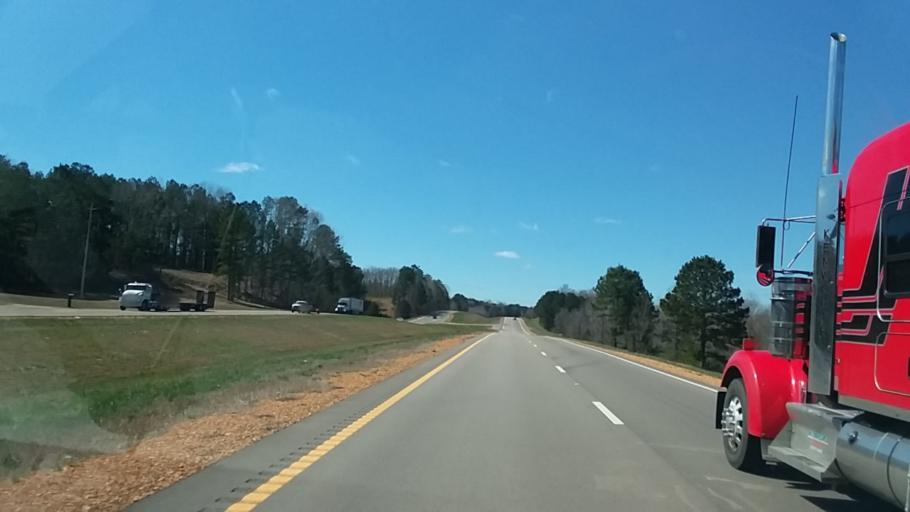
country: US
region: Mississippi
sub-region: Alcorn County
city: Farmington
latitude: 34.8606
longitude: -88.4030
